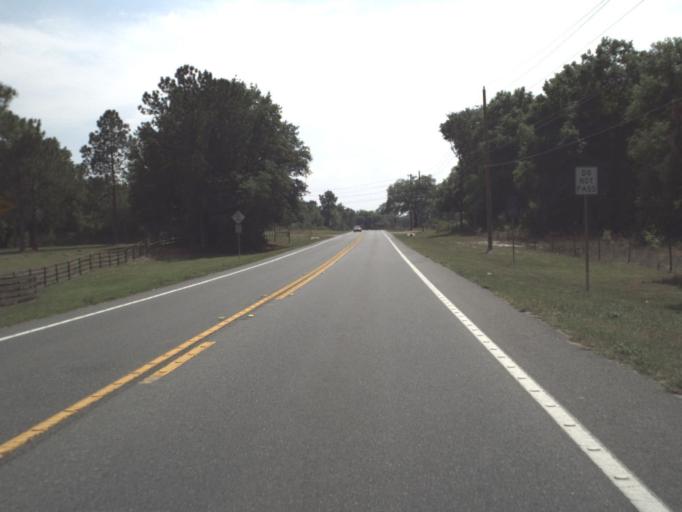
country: US
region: Florida
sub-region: Lake County
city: Howie In The Hills
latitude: 28.6758
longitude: -81.7789
